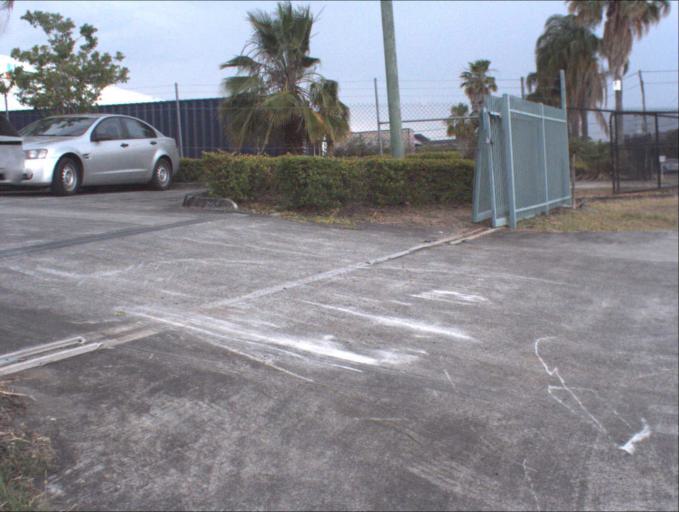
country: AU
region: Queensland
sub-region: Logan
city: Beenleigh
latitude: -27.6810
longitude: 153.1929
